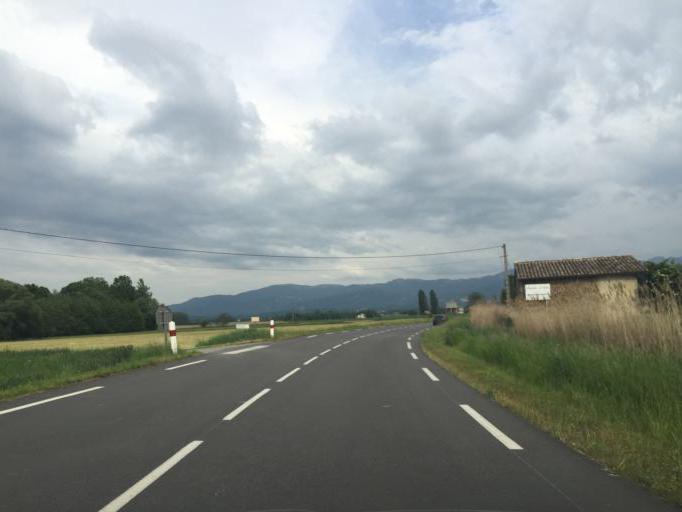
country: FR
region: Rhone-Alpes
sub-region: Departement de la Drome
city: Alixan
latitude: 44.9747
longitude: 5.0366
